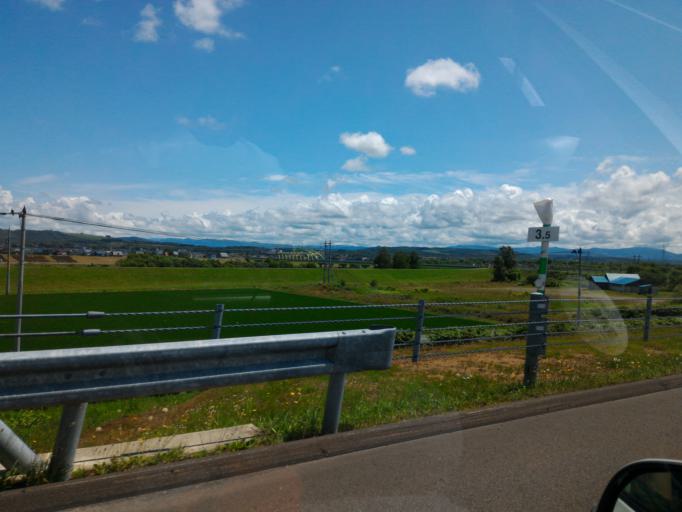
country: JP
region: Hokkaido
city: Nayoro
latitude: 44.3487
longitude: 142.4357
